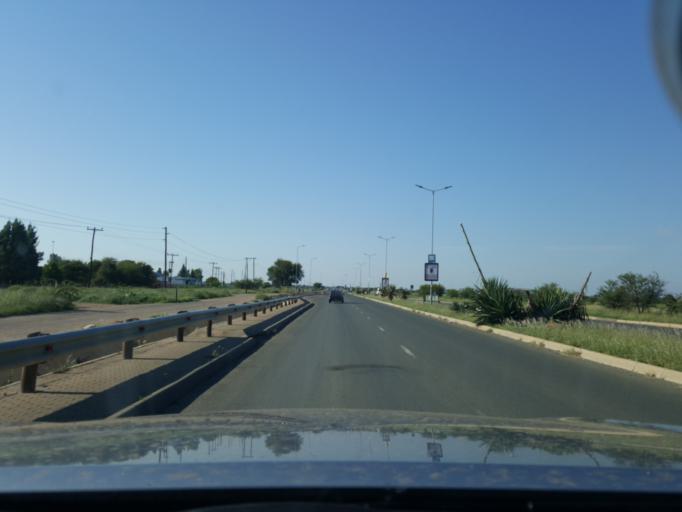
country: ZA
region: North-West
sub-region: Ngaka Modiri Molema District Municipality
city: Mmabatho
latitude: -25.8223
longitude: 25.6350
